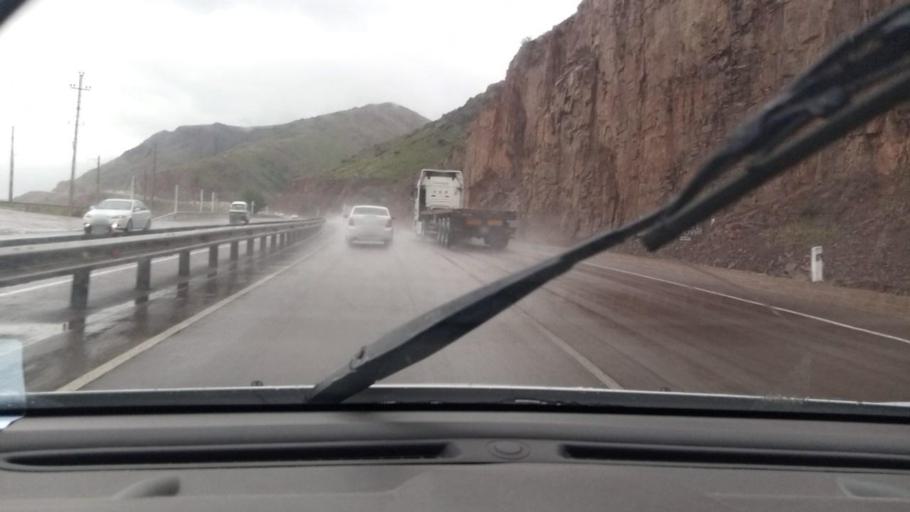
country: UZ
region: Toshkent
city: Angren
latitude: 41.0764
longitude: 70.3050
